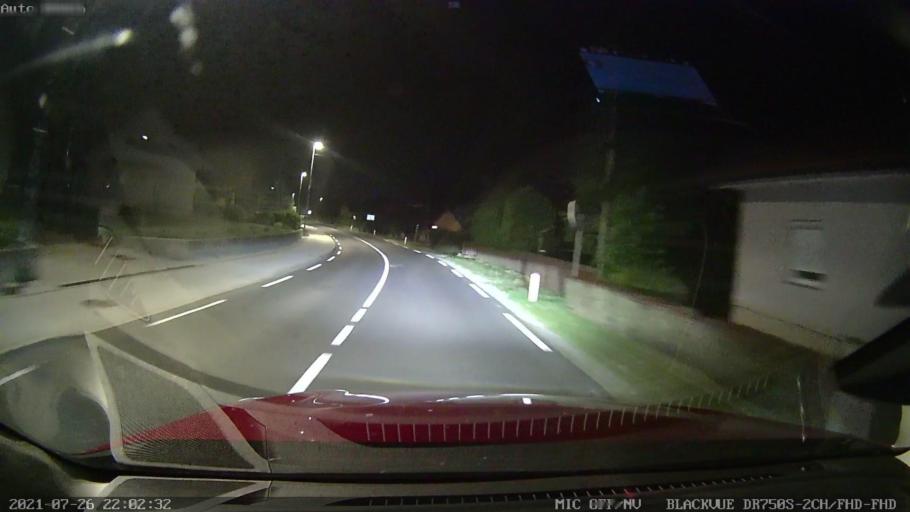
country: SI
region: Markovci
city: Markovci
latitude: 46.3820
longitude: 15.9694
